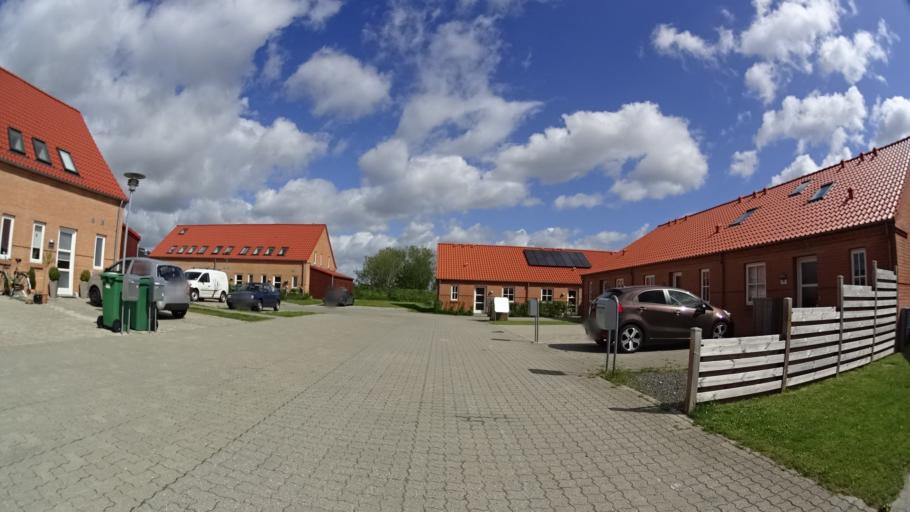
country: DK
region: Central Jutland
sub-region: Arhus Kommune
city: Stavtrup
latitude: 56.1277
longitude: 10.1134
